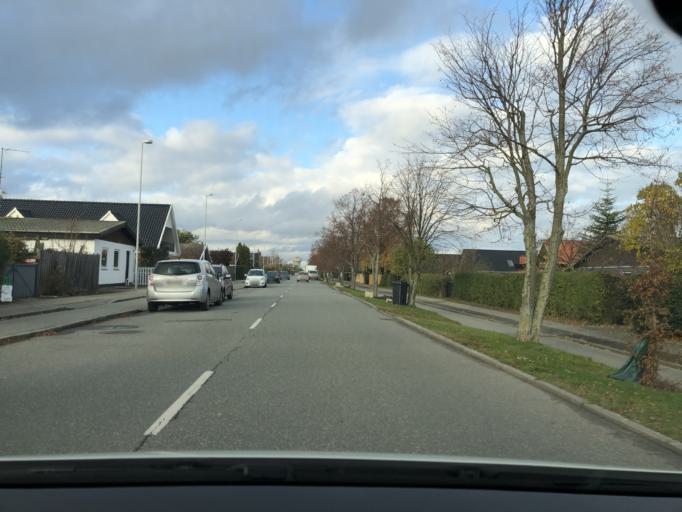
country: DK
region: Capital Region
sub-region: Tarnby Kommune
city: Tarnby
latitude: 55.6112
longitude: 12.5934
